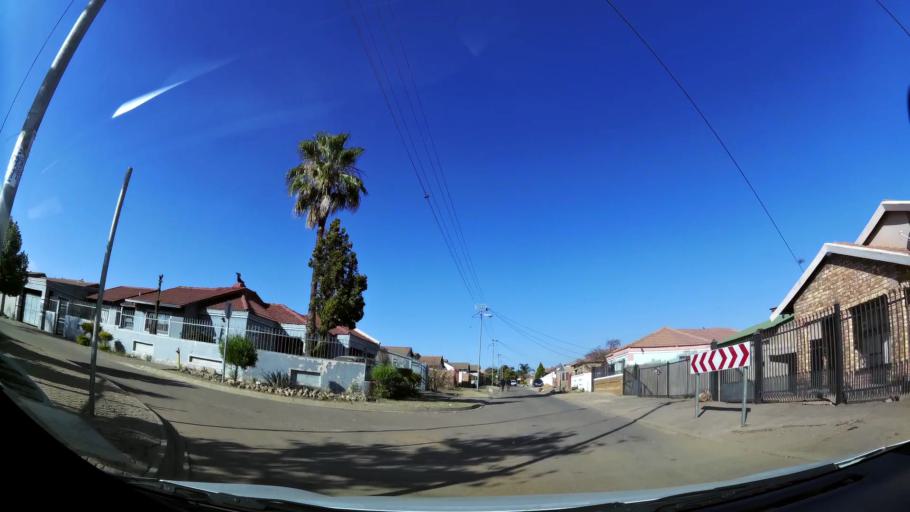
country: ZA
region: Gauteng
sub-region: City of Tshwane Metropolitan Municipality
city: Cullinan
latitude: -25.7190
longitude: 28.3871
